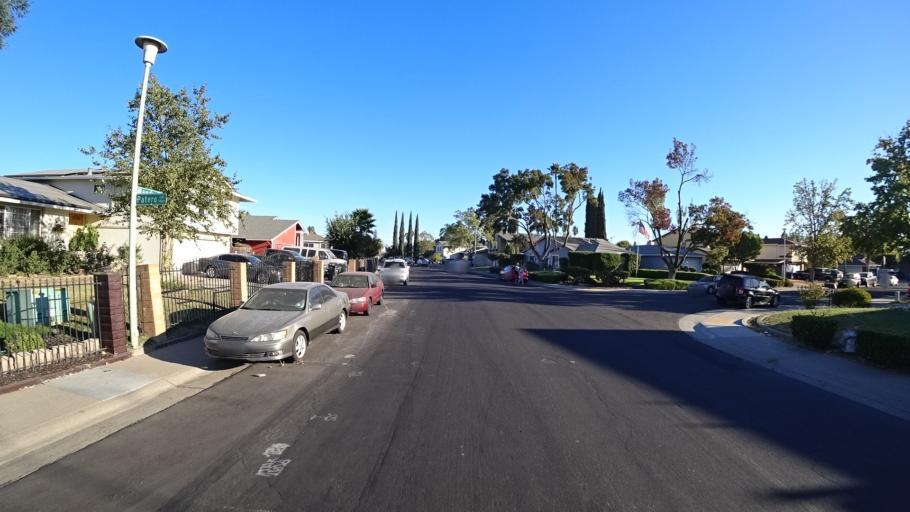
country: US
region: California
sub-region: Sacramento County
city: Parkway
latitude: 38.4880
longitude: -121.4598
